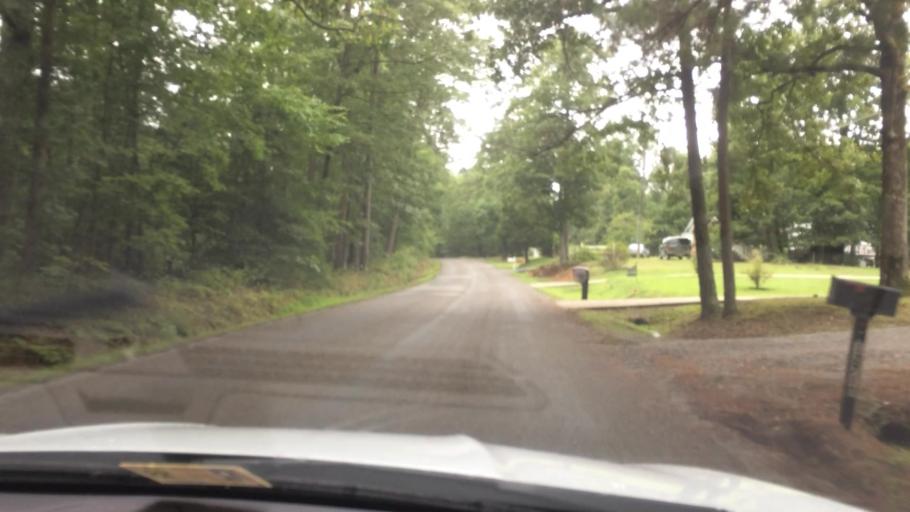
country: US
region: Virginia
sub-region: Charles City County
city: Charles City
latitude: 37.4097
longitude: -77.0483
